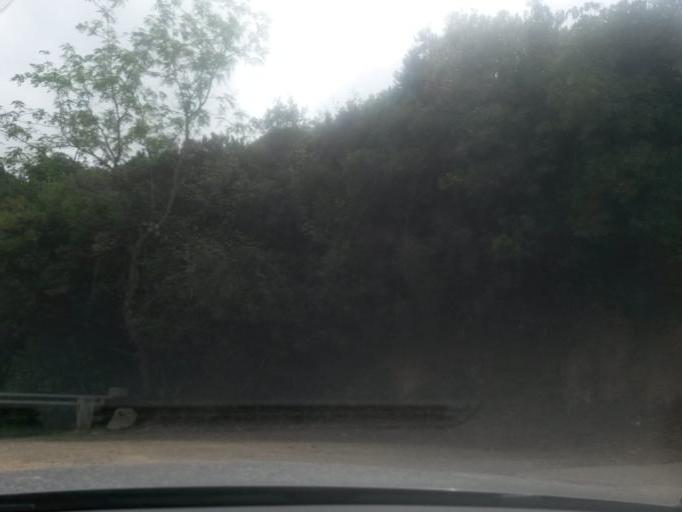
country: IT
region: Tuscany
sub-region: Provincia di Livorno
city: Porto Azzurro
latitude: 42.7423
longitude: 10.4123
